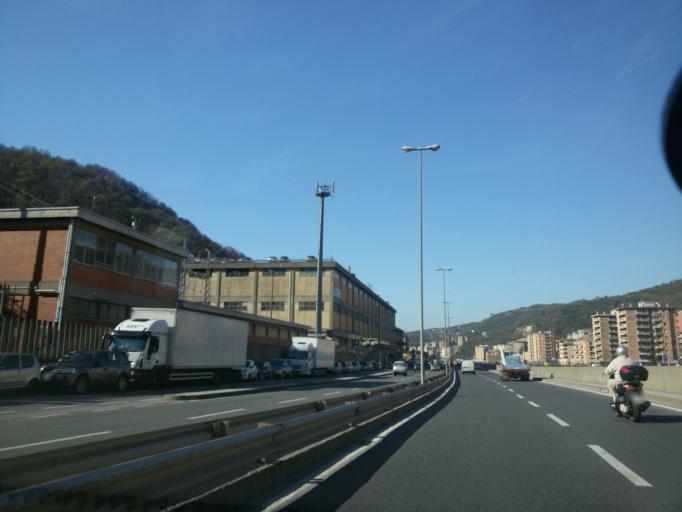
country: IT
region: Liguria
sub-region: Provincia di Genova
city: Piccarello
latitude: 44.4511
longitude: 8.9759
